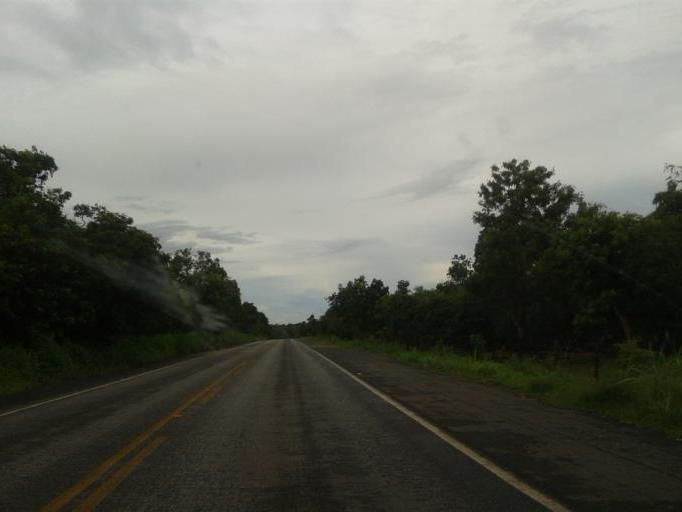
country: BR
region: Goias
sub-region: Mozarlandia
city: Mozarlandia
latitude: -14.8408
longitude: -50.5411
